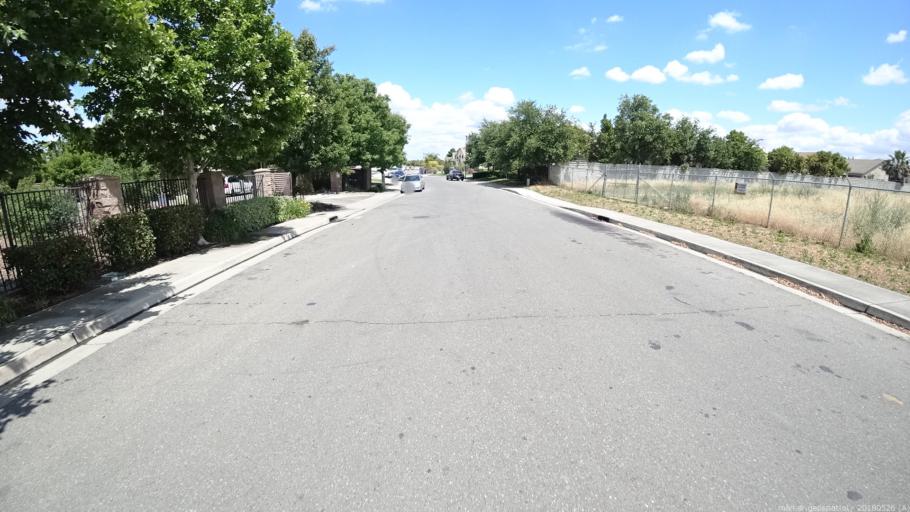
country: US
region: California
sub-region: Sacramento County
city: Sacramento
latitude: 38.6257
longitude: -121.4749
